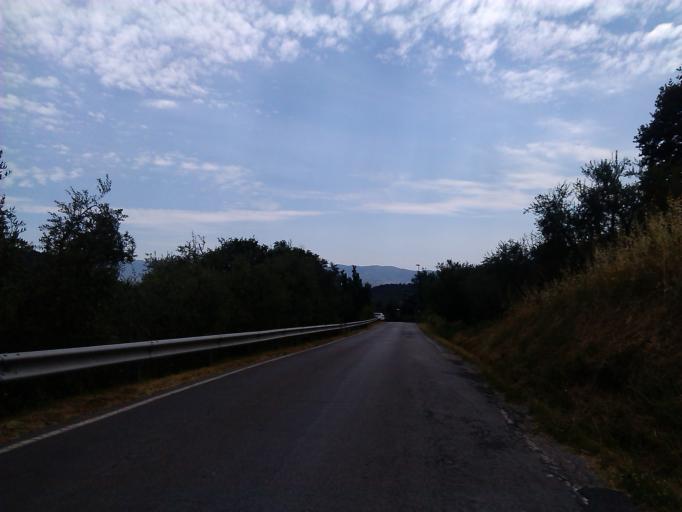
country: IT
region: Tuscany
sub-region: Provincia di Prato
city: Montemurlo
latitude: 43.9584
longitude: 11.0430
